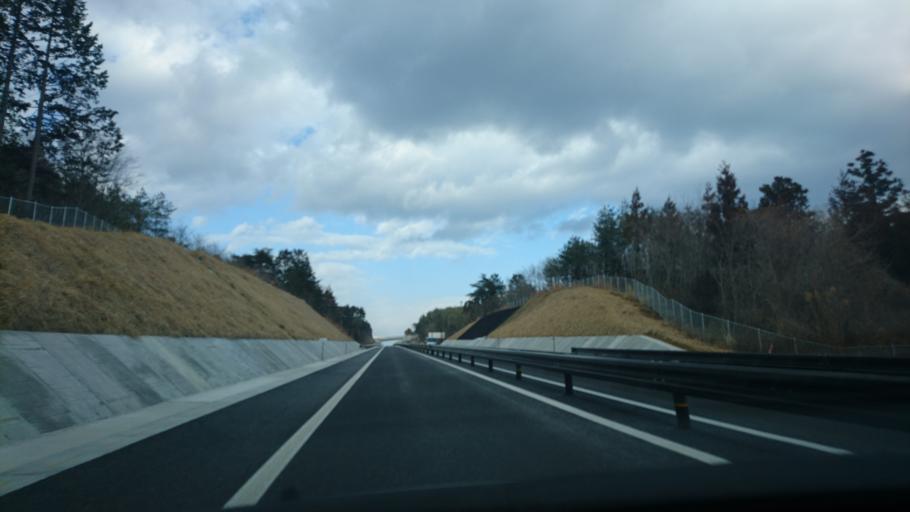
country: JP
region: Miyagi
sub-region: Oshika Gun
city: Onagawa Cho
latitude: 38.7259
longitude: 141.5143
